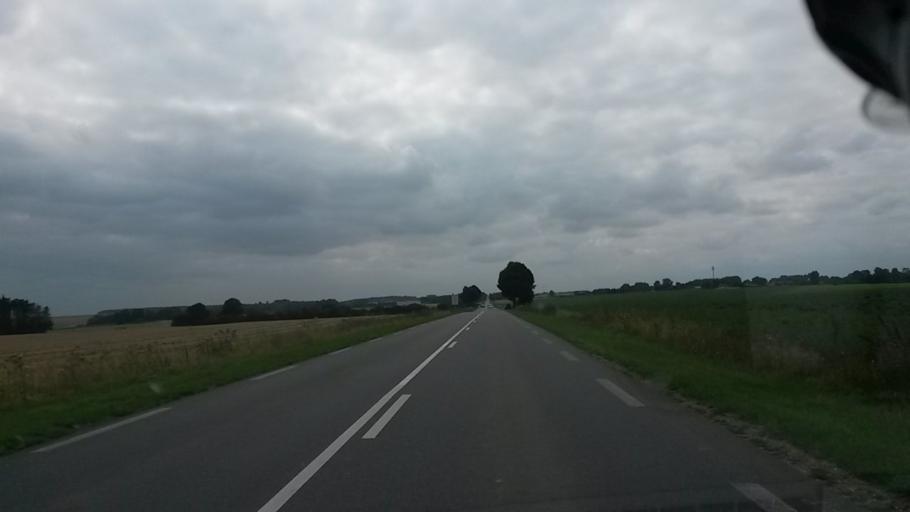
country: FR
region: Picardie
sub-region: Departement de la Somme
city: Corbie
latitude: 49.9666
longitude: 2.5277
